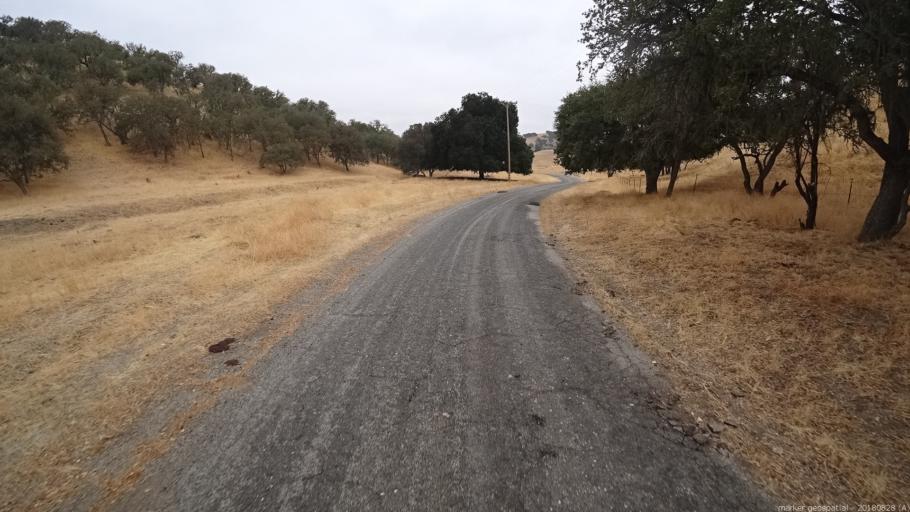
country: US
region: California
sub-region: San Luis Obispo County
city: San Miguel
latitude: 35.9415
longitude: -120.7569
